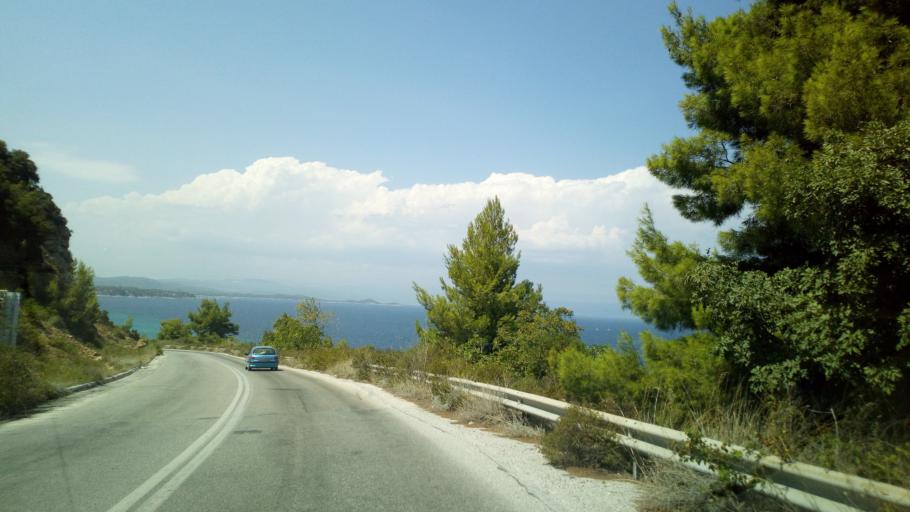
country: GR
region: Central Macedonia
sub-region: Nomos Chalkidikis
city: Neos Marmaras
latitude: 40.1722
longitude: 23.8588
